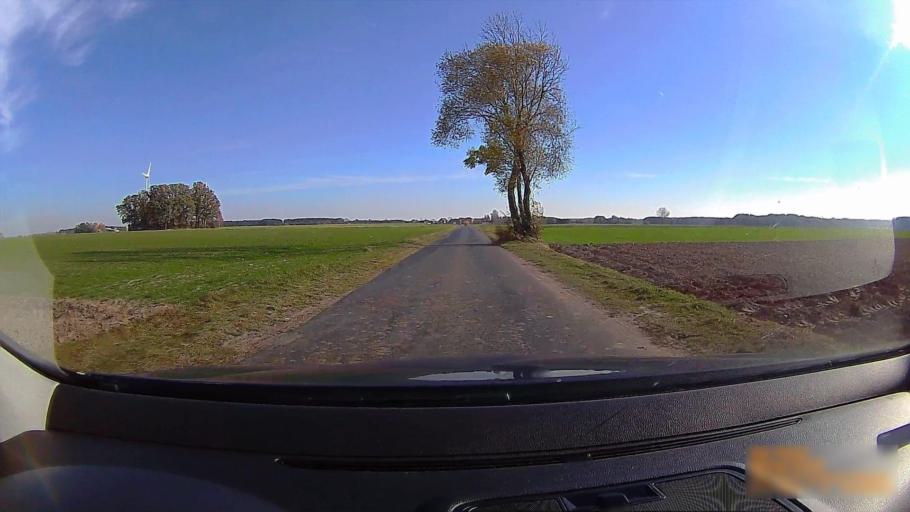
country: PL
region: Greater Poland Voivodeship
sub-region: Powiat ostrzeszowski
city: Doruchow
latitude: 51.3948
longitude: 18.0381
